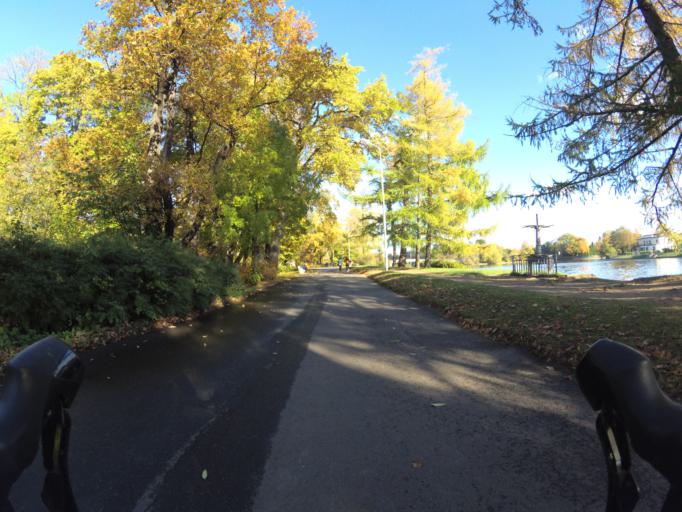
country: RU
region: Leningrad
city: Krestovskiy ostrov
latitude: 59.9759
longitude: 30.2680
